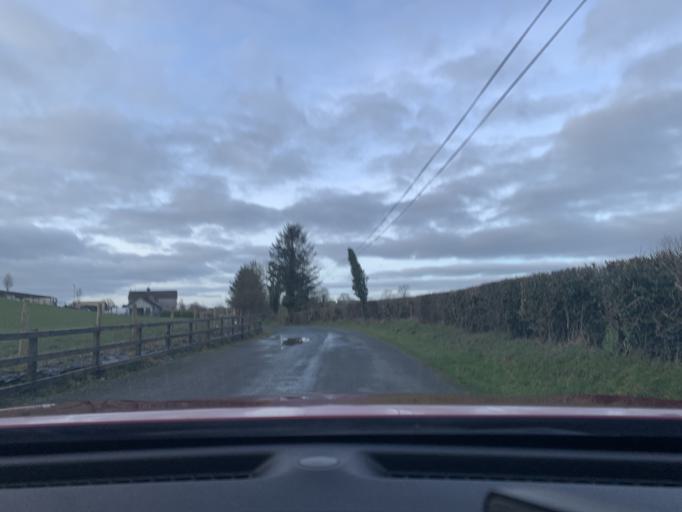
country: IE
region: Connaught
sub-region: Sligo
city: Ballymote
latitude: 54.0607
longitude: -8.5649
